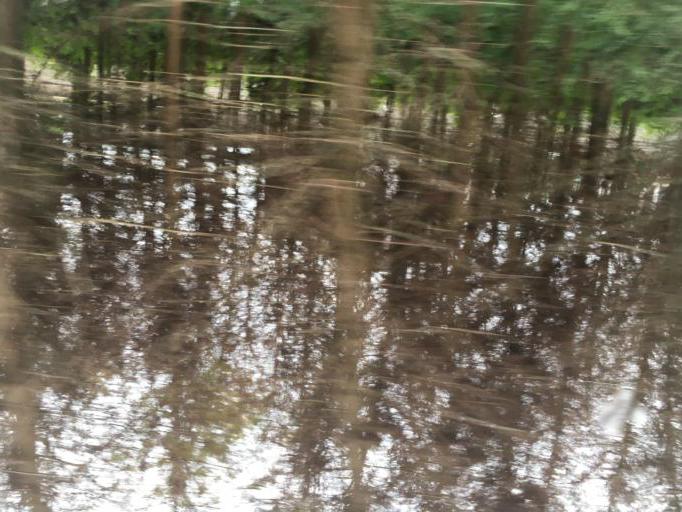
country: TW
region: Taiwan
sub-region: Yilan
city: Yilan
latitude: 24.7441
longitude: 121.7795
